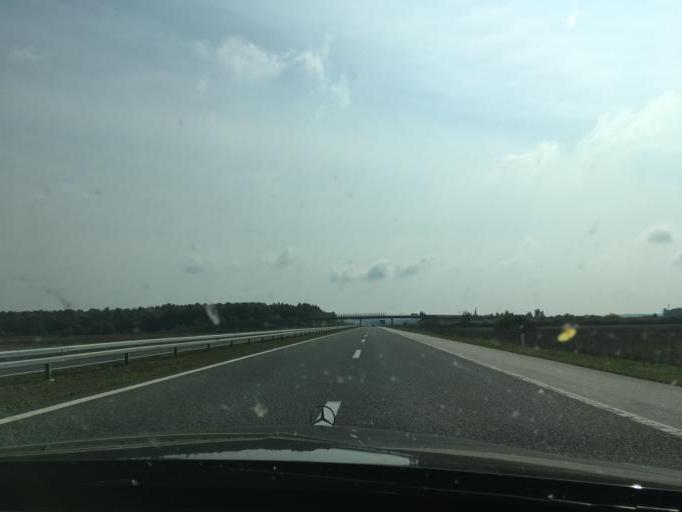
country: HR
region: Vukovarsko-Srijemska
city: Bosnjaci
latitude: 45.0724
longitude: 18.7844
